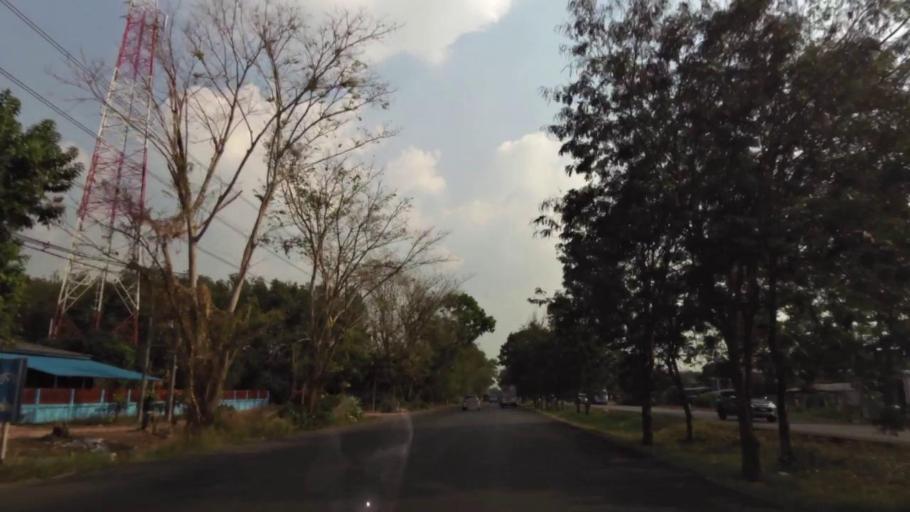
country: TH
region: Rayong
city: Wang Chan
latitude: 12.8908
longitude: 101.5500
